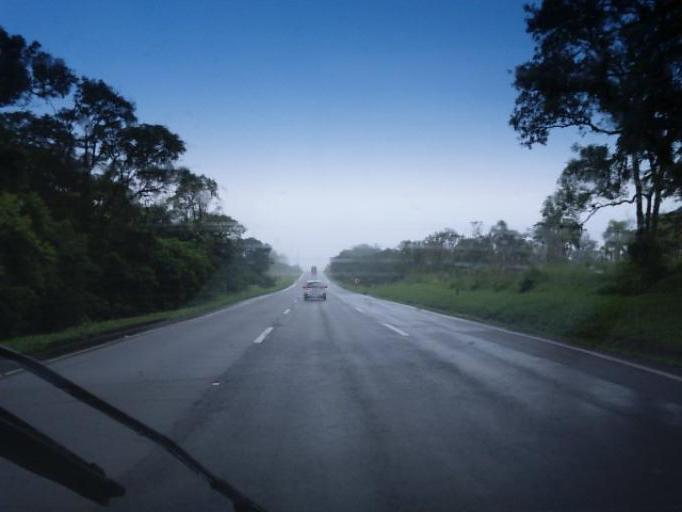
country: BR
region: Parana
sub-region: Antonina
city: Antonina
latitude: -25.1117
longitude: -48.7780
